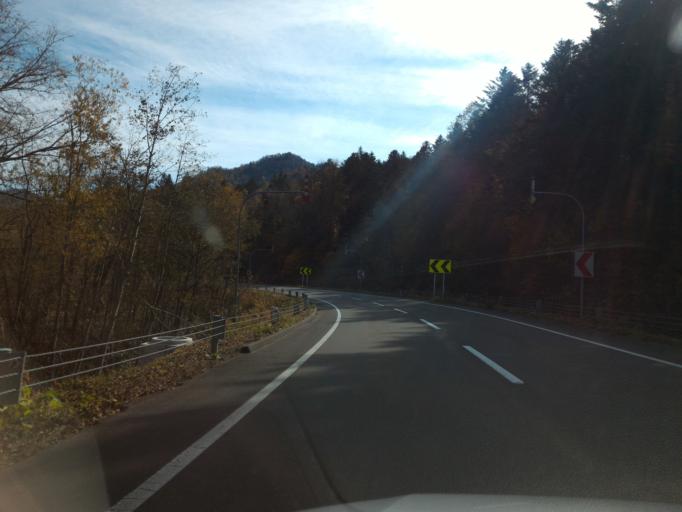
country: JP
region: Hokkaido
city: Ashibetsu
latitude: 43.3699
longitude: 142.2247
